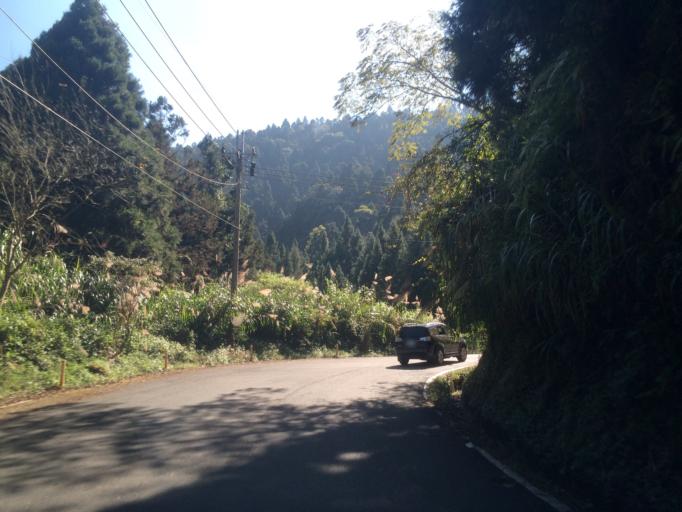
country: TW
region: Taiwan
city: Lugu
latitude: 23.6618
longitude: 120.7724
